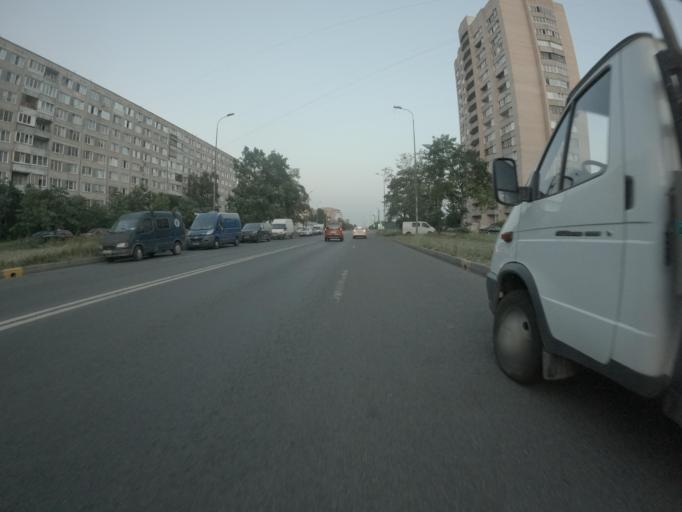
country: RU
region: St.-Petersburg
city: Krasnogvargeisky
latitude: 59.9164
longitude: 30.4838
